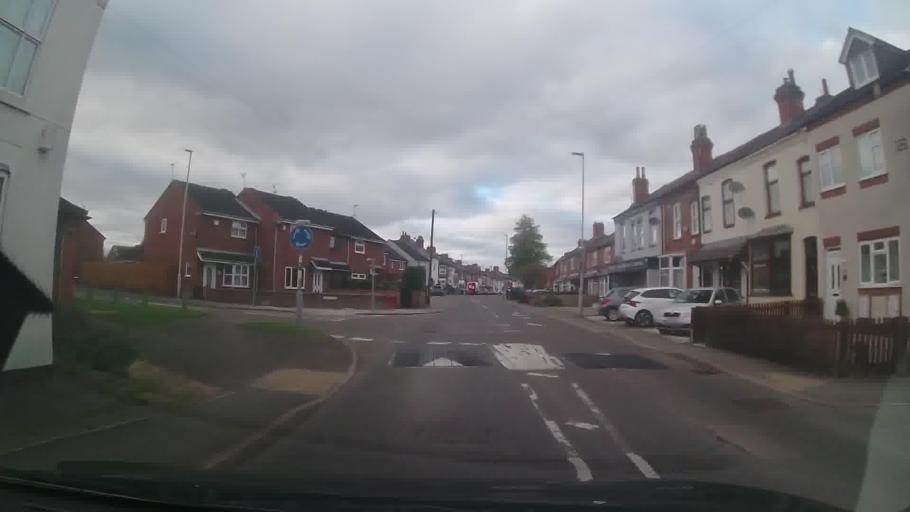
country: GB
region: England
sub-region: Leicestershire
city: Kirby Muxloe
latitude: 52.6444
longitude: -1.2391
